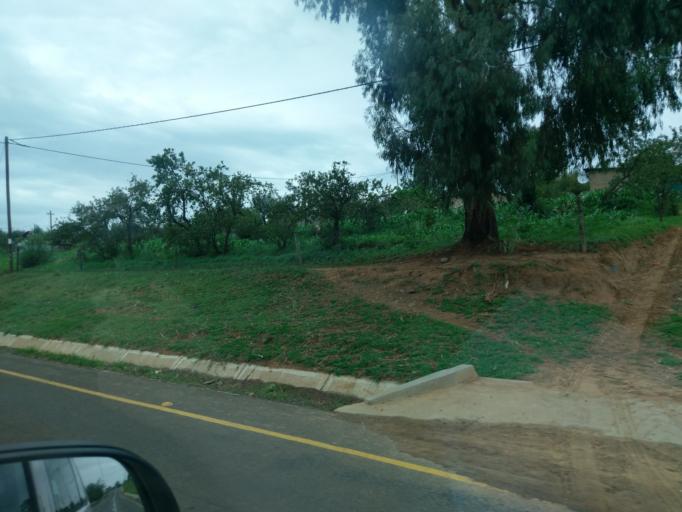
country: LS
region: Berea
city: Teyateyaneng
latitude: -29.1302
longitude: 27.9852
